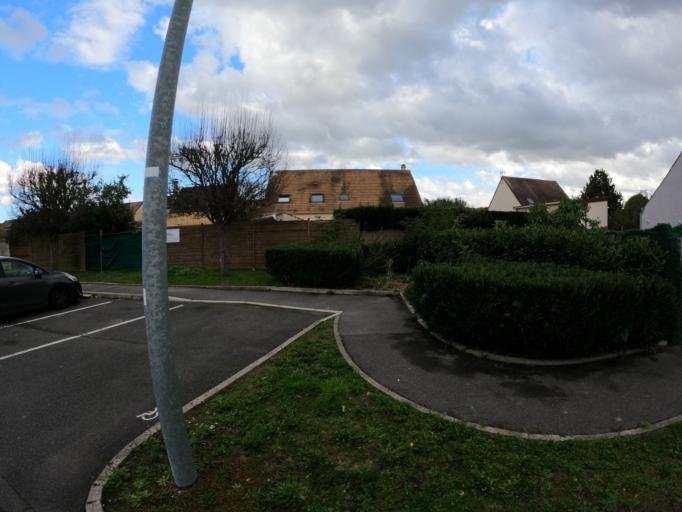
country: FR
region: Ile-de-France
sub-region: Departement de Seine-et-Marne
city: Esbly
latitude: 48.8997
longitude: 2.8088
